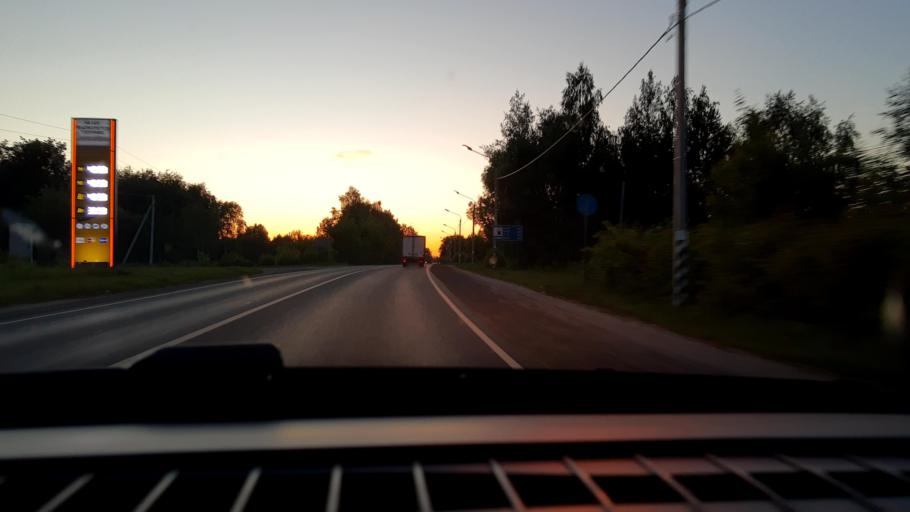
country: RU
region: Nizjnij Novgorod
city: Gorodets
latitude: 56.6009
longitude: 43.4515
